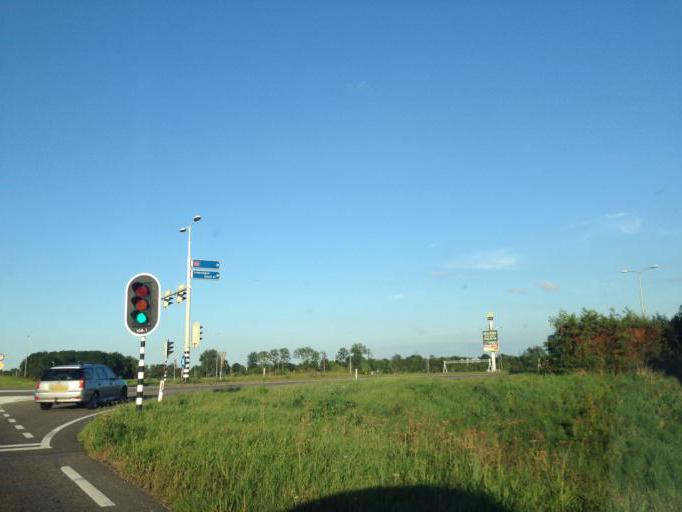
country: NL
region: Gelderland
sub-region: Gemeente Zaltbommel
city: Zaltbommel
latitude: 51.8773
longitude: 5.2062
